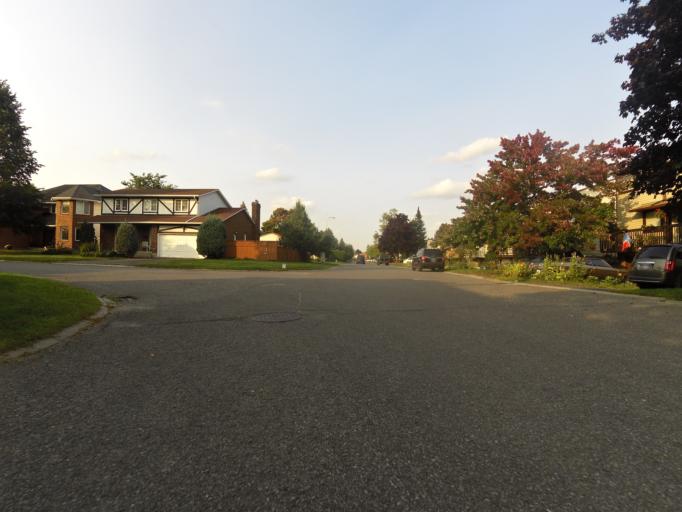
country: CA
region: Ontario
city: Bells Corners
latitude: 45.2813
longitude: -75.7515
